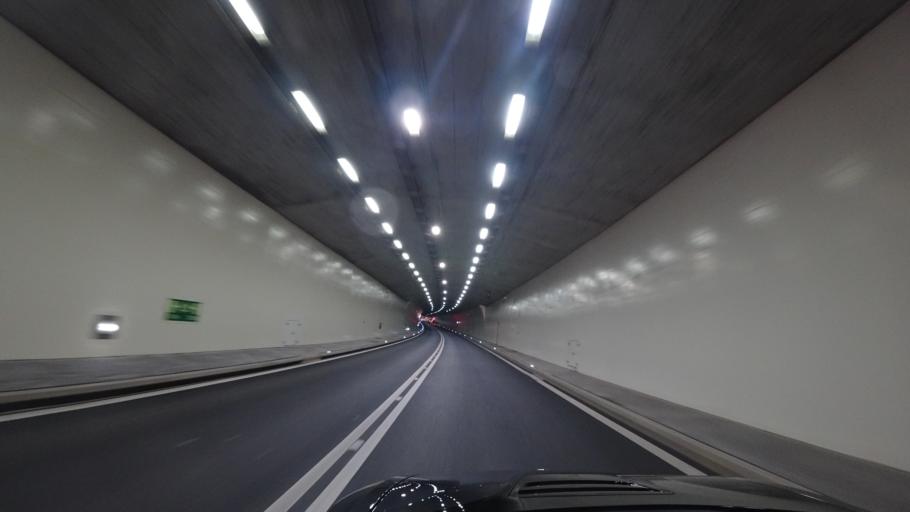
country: CH
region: Obwalden
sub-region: Obwalden
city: Lungern
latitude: 46.8018
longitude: 8.1700
